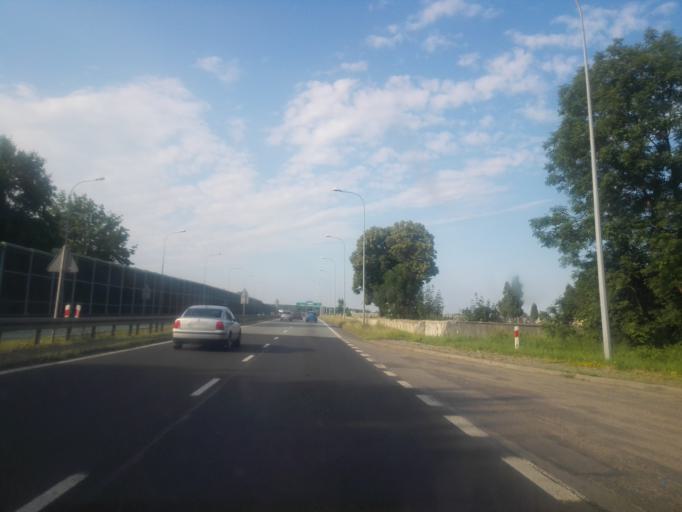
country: PL
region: Silesian Voivodeship
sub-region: Powiat bedzinski
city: Siewierz
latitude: 50.4134
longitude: 19.2052
